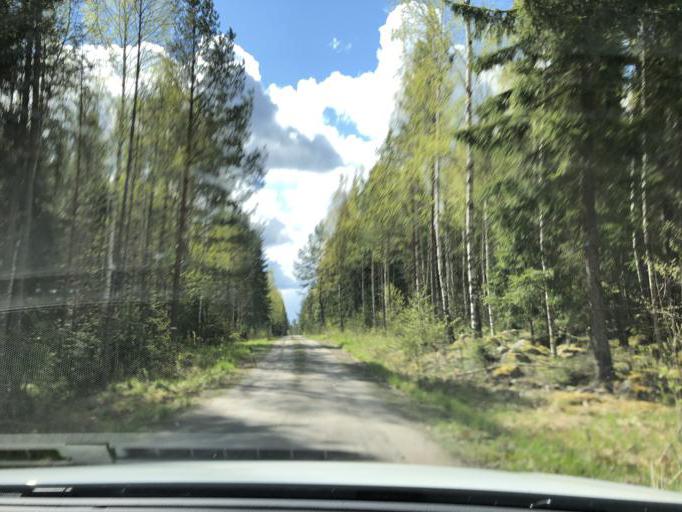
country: SE
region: Uppsala
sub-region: Heby Kommun
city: Tarnsjo
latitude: 60.2507
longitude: 16.9005
